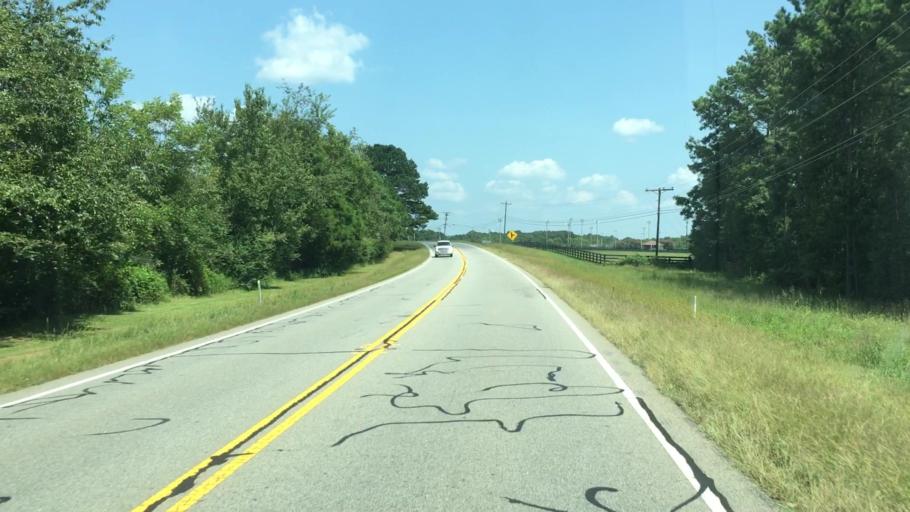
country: US
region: Georgia
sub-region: Oconee County
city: Watkinsville
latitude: 33.8671
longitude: -83.4849
